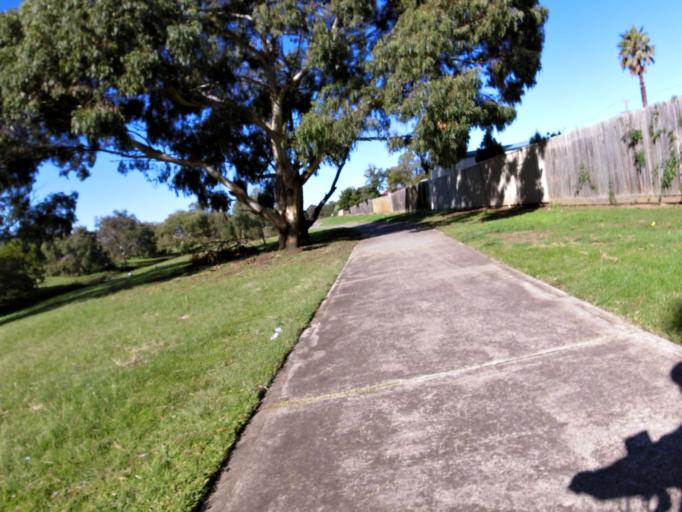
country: AU
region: Victoria
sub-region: Wyndham
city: Tarneit
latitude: -37.8775
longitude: 144.6751
